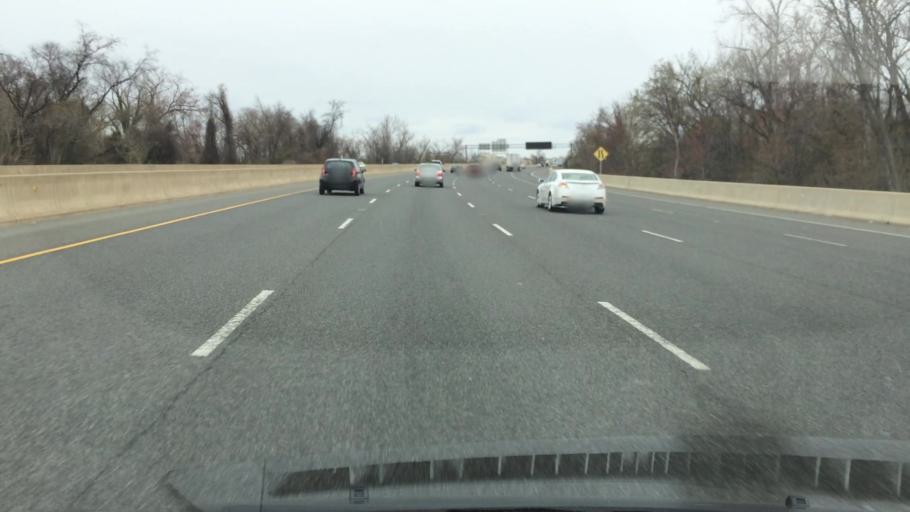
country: US
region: Maryland
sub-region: Prince George's County
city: Forest Heights
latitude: 38.8026
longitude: -77.0216
